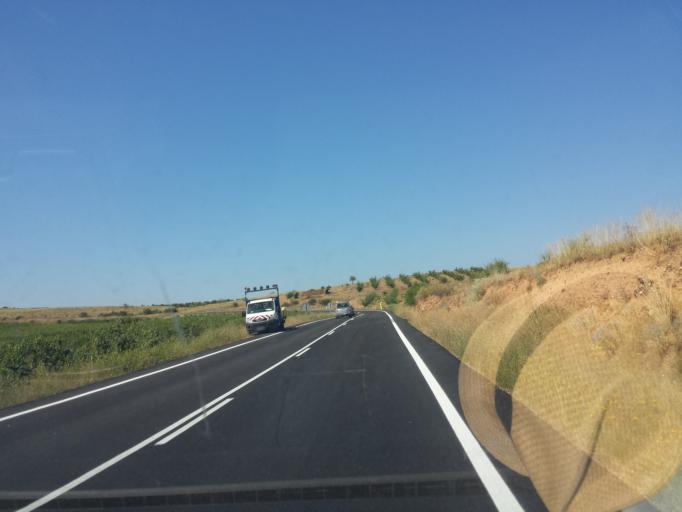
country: ES
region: Aragon
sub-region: Provincia de Zaragoza
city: Munebrega
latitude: 41.2312
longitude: -1.7282
